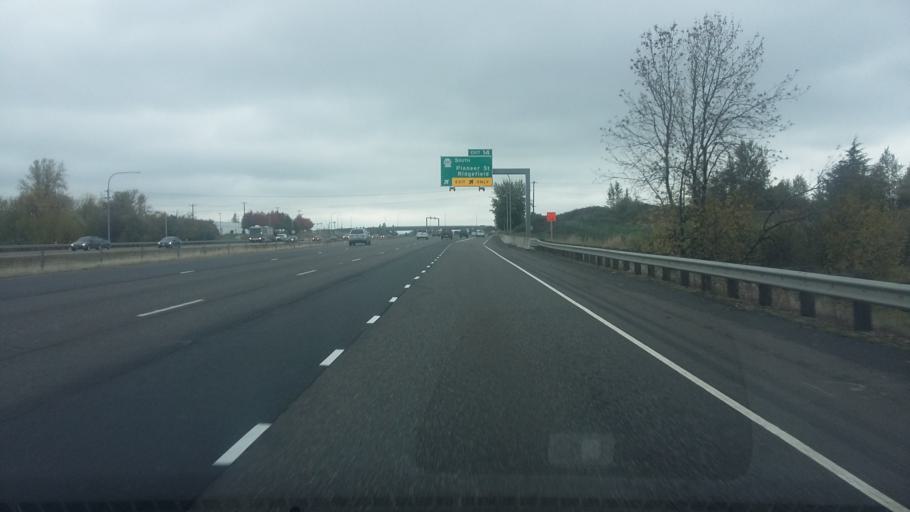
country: US
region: Washington
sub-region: Clark County
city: La Center
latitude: 45.8101
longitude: -122.6830
